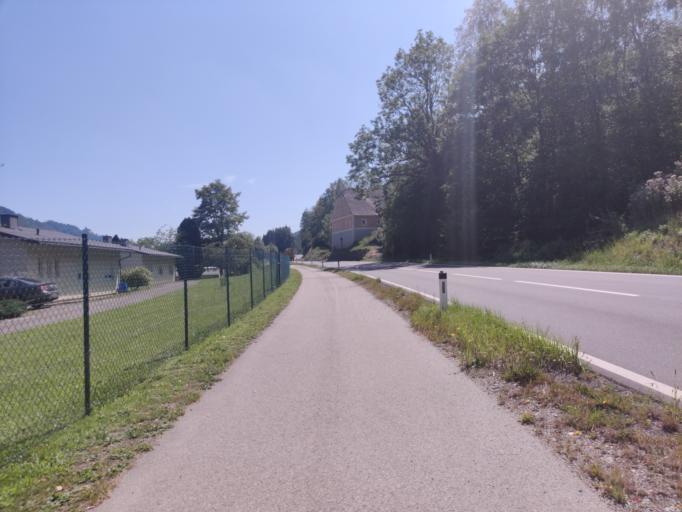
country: AT
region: Upper Austria
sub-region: Politischer Bezirk Rohrbach
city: Pfarrkirchen im Muehlkreis
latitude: 48.4913
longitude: 13.7423
